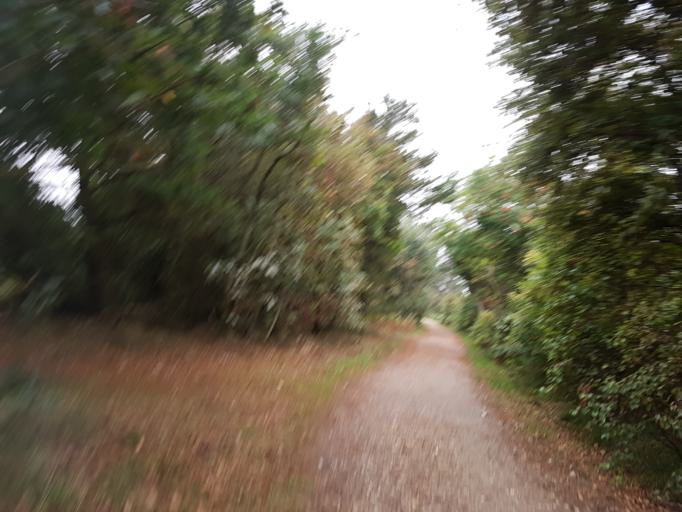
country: DK
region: Central Jutland
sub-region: Ringkobing-Skjern Kommune
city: Hvide Sande
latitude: 55.8522
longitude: 8.2864
